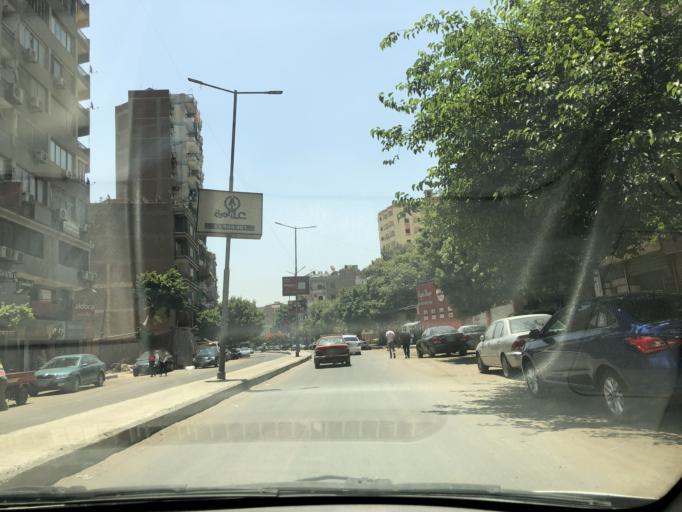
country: EG
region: Muhafazat al Qahirah
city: Cairo
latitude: 30.0693
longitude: 31.2706
